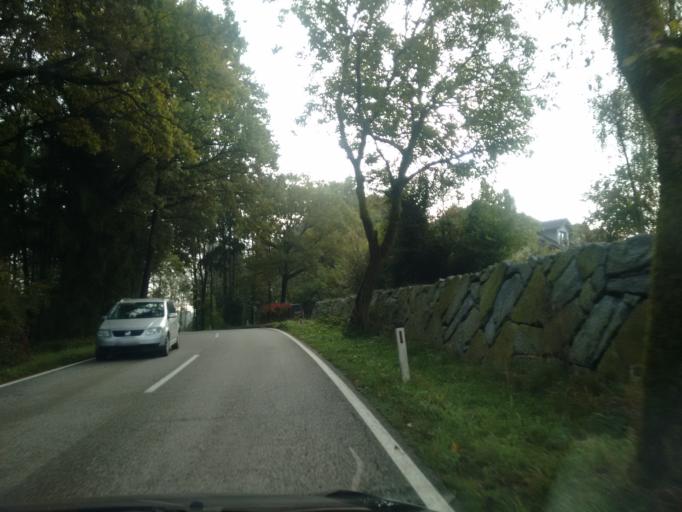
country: AT
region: Upper Austria
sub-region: Wels-Land
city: Gunskirchen
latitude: 48.1833
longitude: 13.9696
